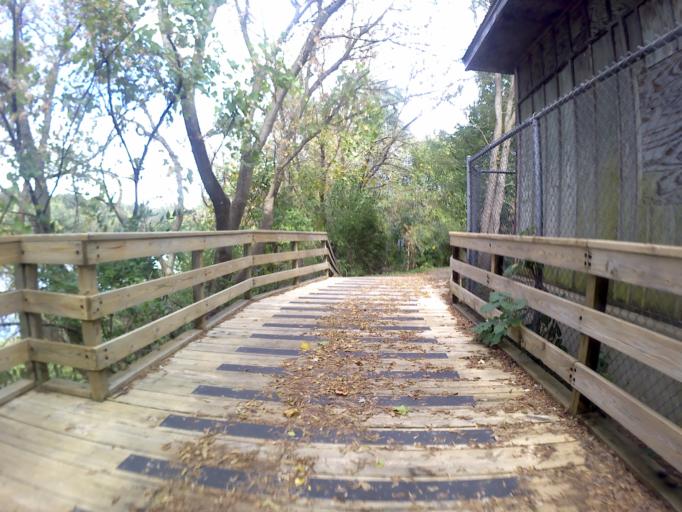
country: US
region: Illinois
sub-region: Kane County
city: Batavia
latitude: 41.8368
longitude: -88.3084
